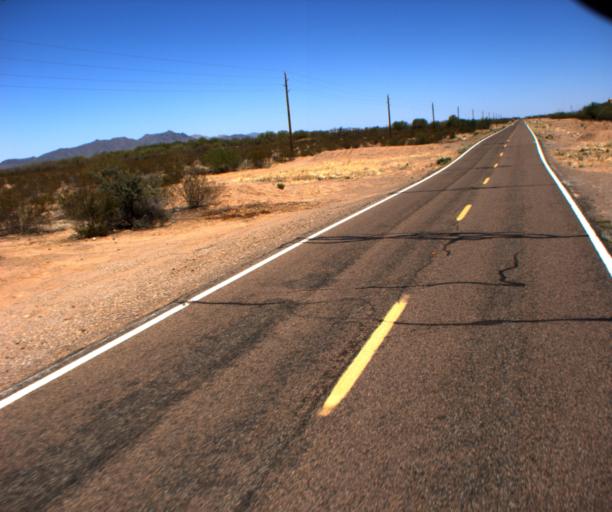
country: US
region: Arizona
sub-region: Pima County
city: Ajo
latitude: 32.2524
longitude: -112.7315
